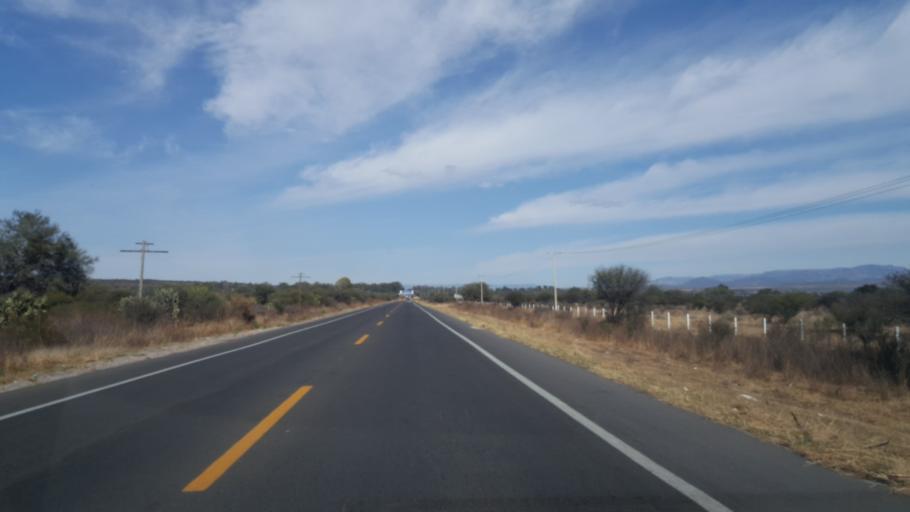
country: MX
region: Jalisco
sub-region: Lagos de Moreno
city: Cristeros [Fraccionamiento]
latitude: 21.2655
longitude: -101.9446
